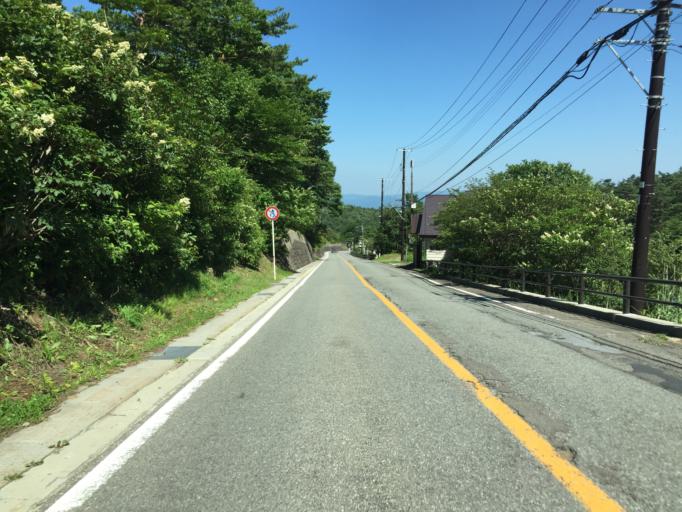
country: JP
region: Fukushima
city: Fukushima-shi
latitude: 37.7530
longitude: 140.3079
